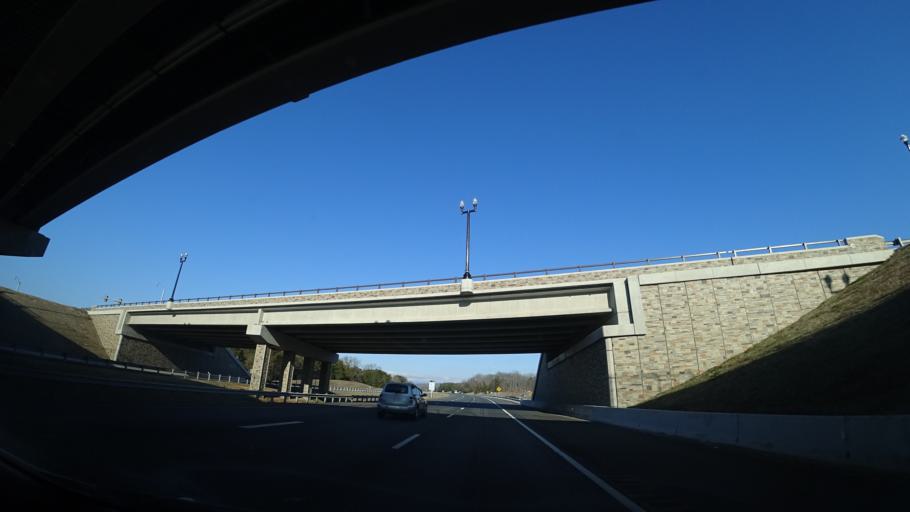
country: US
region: Virginia
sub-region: Prince William County
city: Haymarket
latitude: 38.8180
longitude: -77.6396
